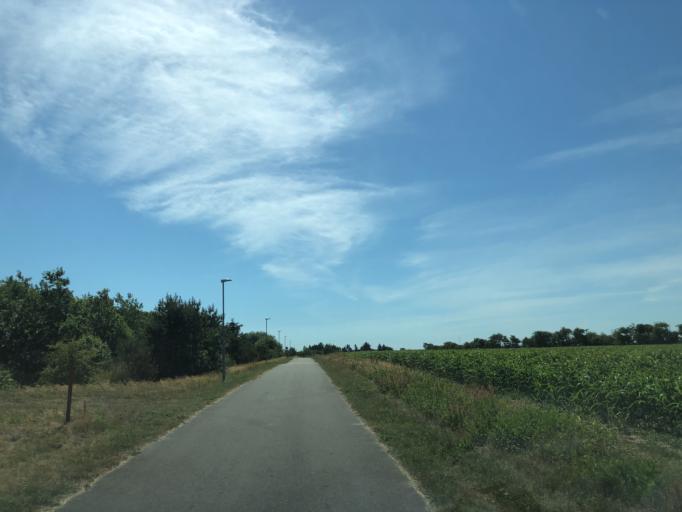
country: DK
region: Central Jutland
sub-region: Skive Kommune
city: Skive
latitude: 56.5424
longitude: 9.0095
